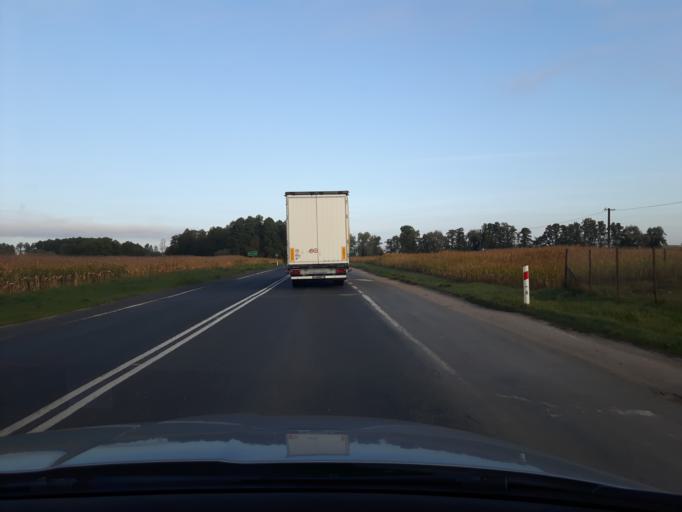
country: PL
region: Masovian Voivodeship
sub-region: Powiat plonski
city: Plonsk
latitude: 52.6788
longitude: 20.3673
